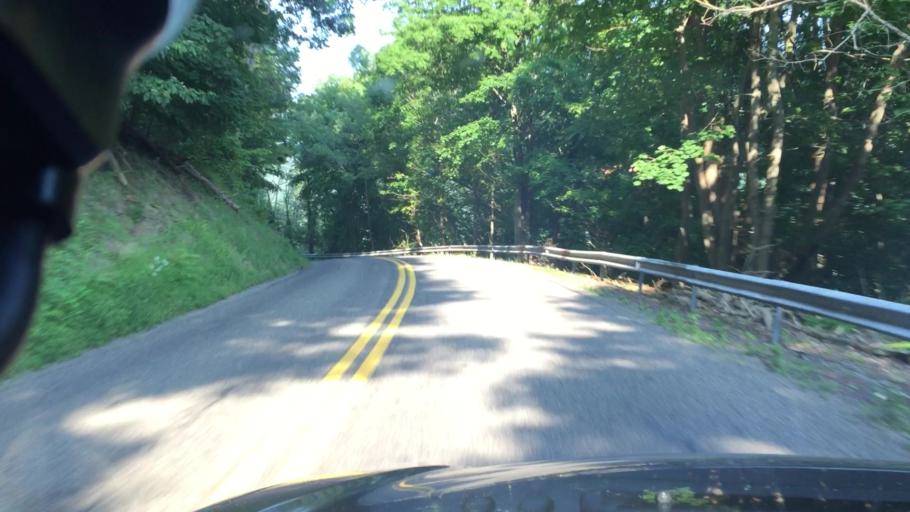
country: US
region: Pennsylvania
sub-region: Columbia County
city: Catawissa
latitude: 40.9517
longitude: -76.4518
